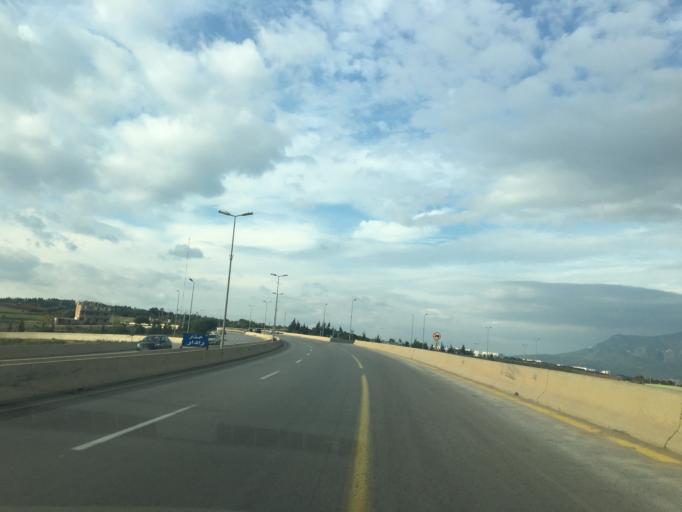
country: DZ
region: Tipaza
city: Tipasa
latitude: 36.5769
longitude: 2.5036
